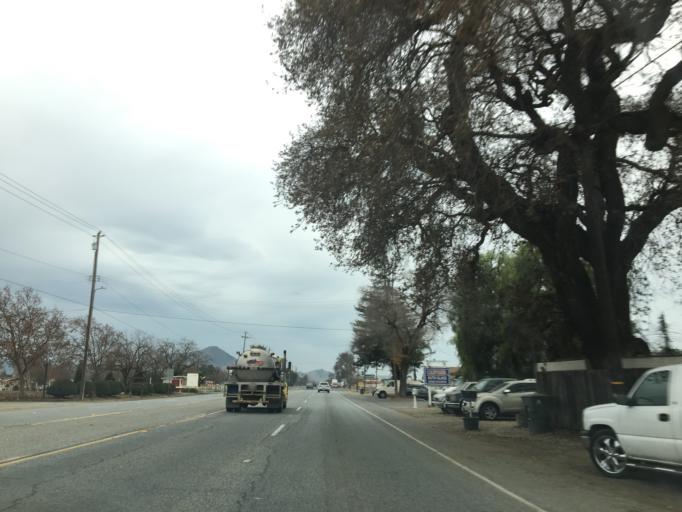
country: US
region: California
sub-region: Santa Clara County
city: San Martin
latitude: 37.0992
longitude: -121.6216
